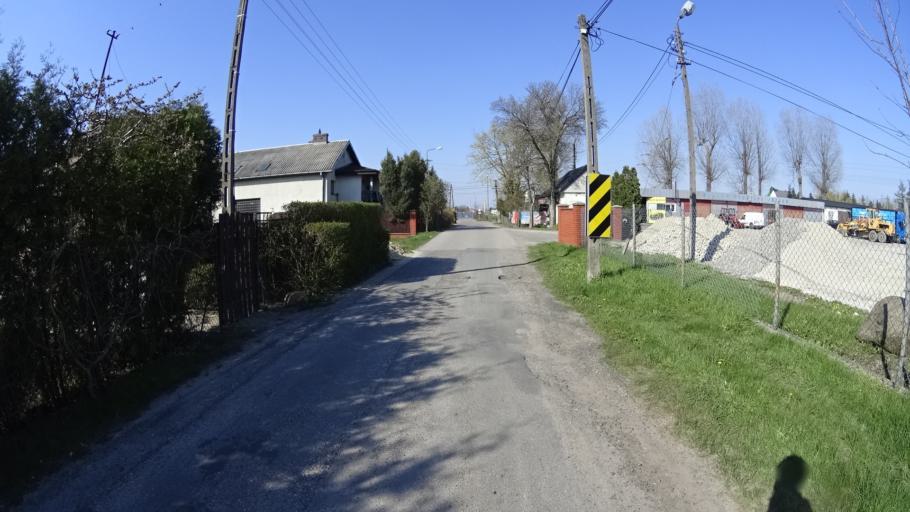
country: PL
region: Masovian Voivodeship
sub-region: Powiat warszawski zachodni
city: Stare Babice
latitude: 52.2483
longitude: 20.8339
